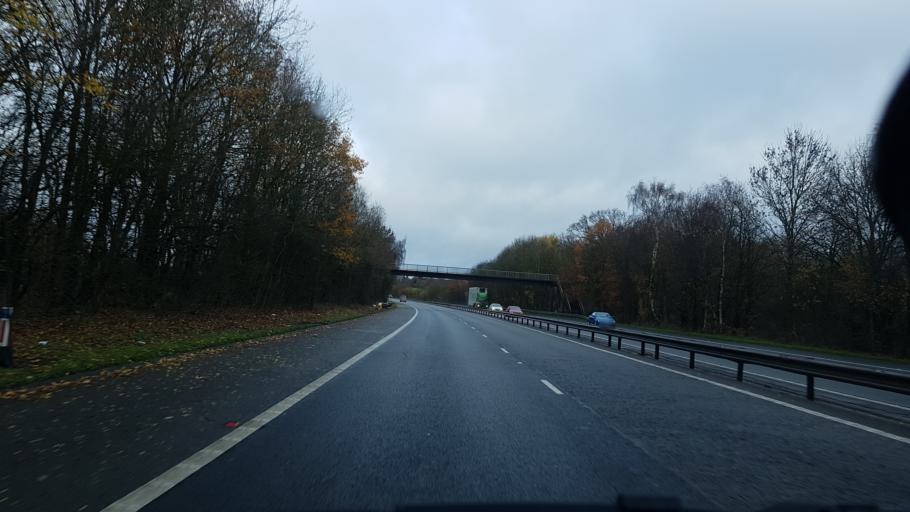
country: GB
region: England
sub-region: Wokingham
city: Wokingham
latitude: 51.4213
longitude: -0.8135
